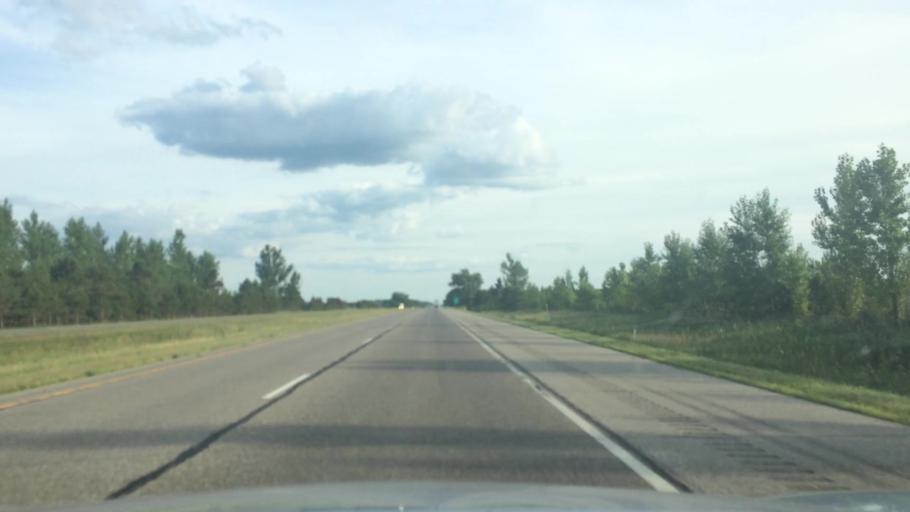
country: US
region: Wisconsin
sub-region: Portage County
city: Plover
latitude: 44.2831
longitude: -89.5237
